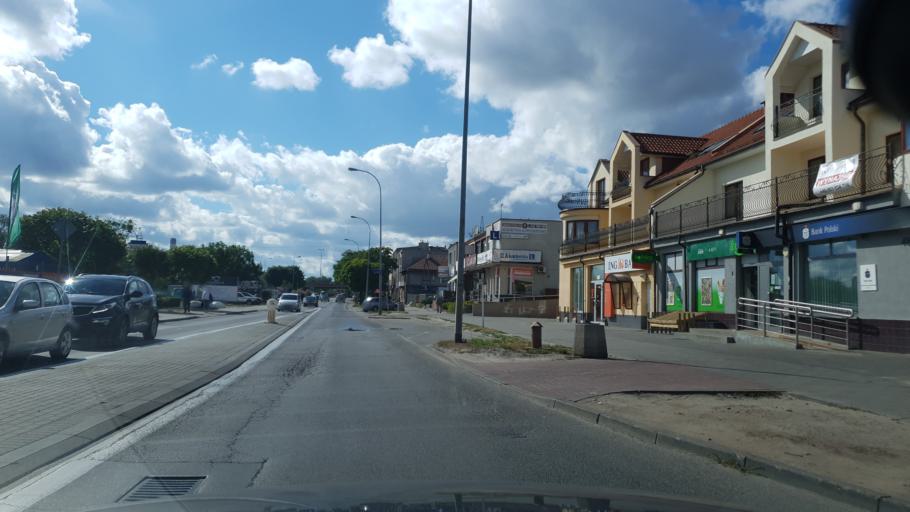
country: PL
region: Pomeranian Voivodeship
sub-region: Gdynia
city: Pogorze
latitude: 54.5502
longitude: 18.5119
